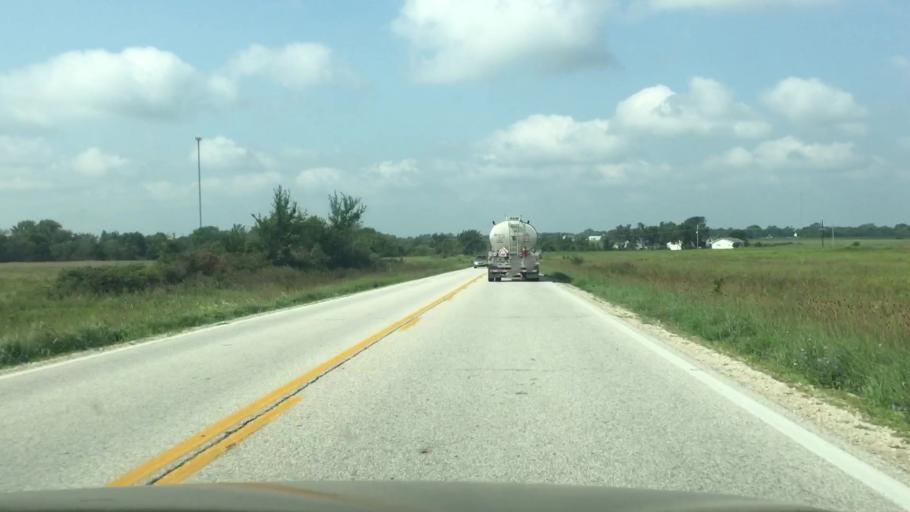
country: US
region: Kansas
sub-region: Anderson County
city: Garnett
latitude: 38.1751
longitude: -95.2748
